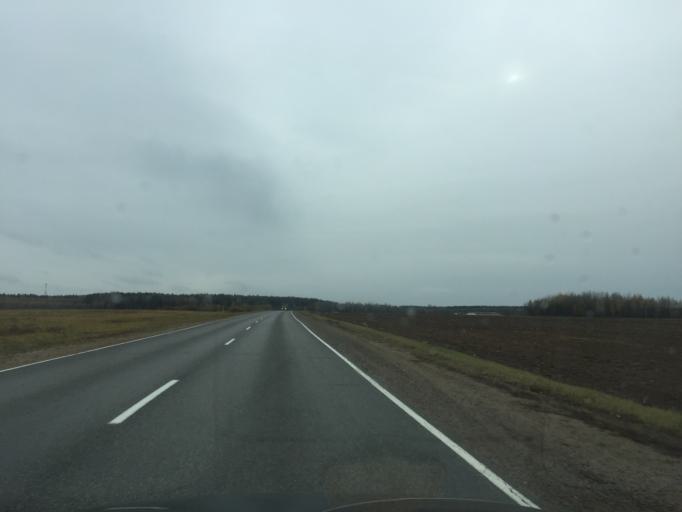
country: BY
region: Mogilev
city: Chavusy
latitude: 53.7449
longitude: 31.0997
